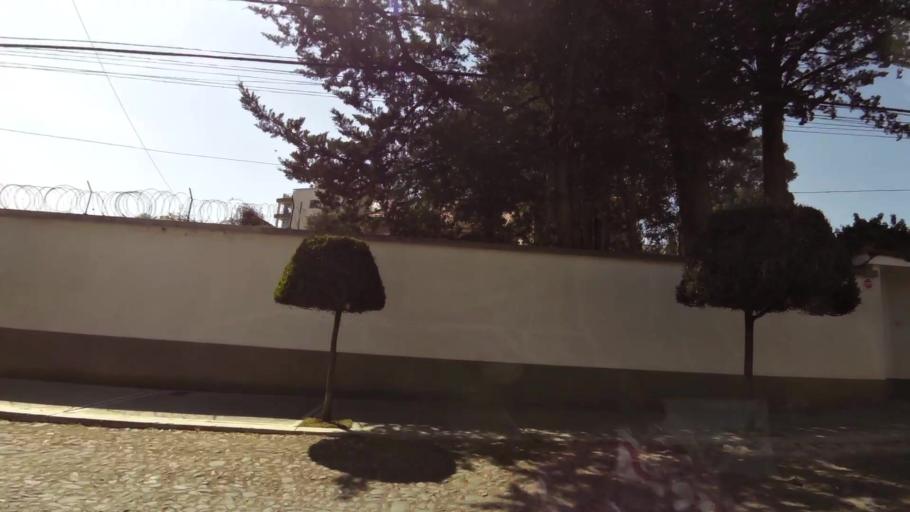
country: BO
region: La Paz
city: La Paz
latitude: -16.5439
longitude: -68.0657
